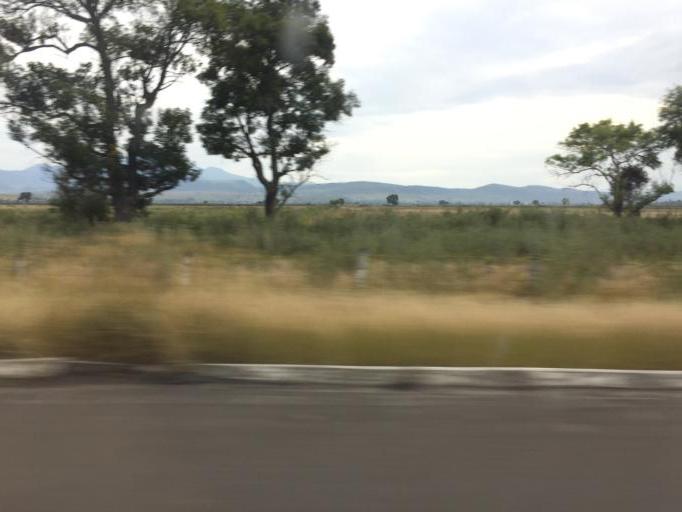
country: MX
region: Mexico
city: Huaniqueo de Morales
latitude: 19.8907
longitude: -101.5300
